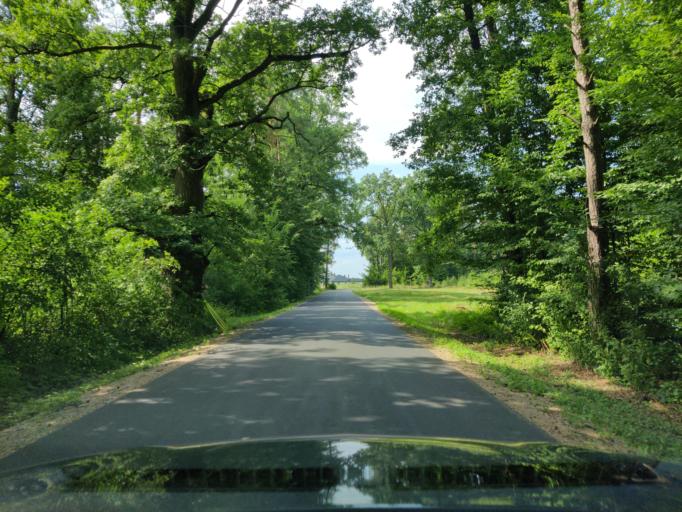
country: PL
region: Masovian Voivodeship
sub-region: Powiat pultuski
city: Obryte
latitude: 52.6914
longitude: 21.2115
